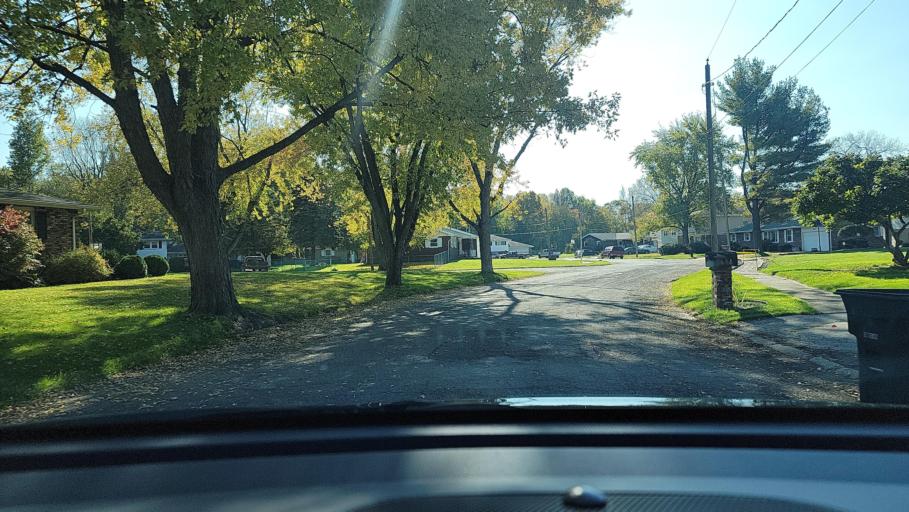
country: US
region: Indiana
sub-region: Porter County
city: Portage
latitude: 41.5753
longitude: -87.1597
